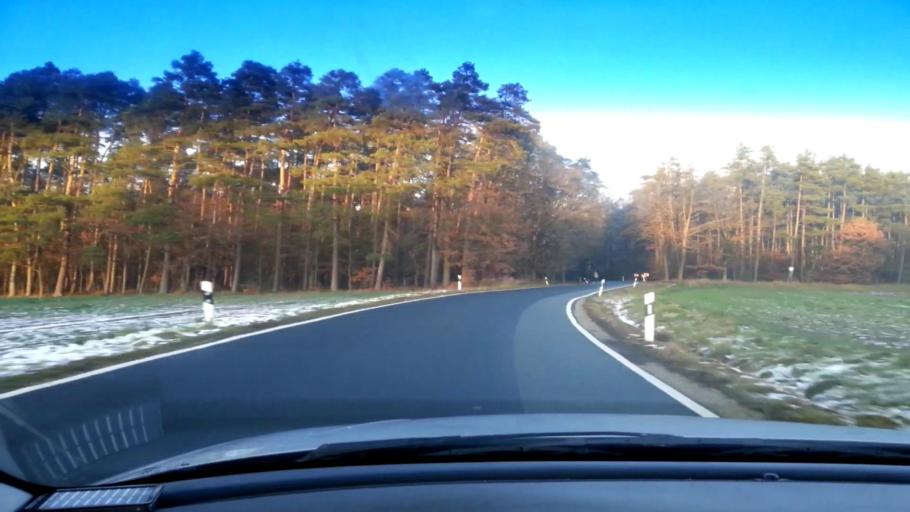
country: DE
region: Bavaria
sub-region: Upper Franconia
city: Pommersfelden
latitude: 49.7435
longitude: 10.8543
